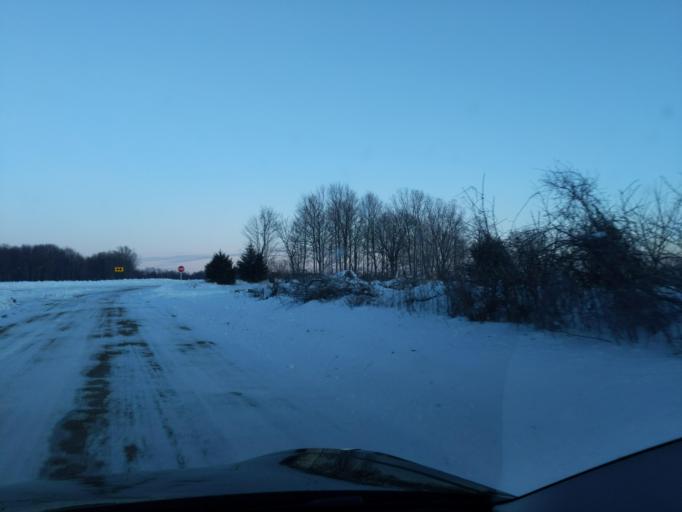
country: US
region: Michigan
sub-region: Ingham County
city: Williamston
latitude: 42.5704
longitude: -84.3153
